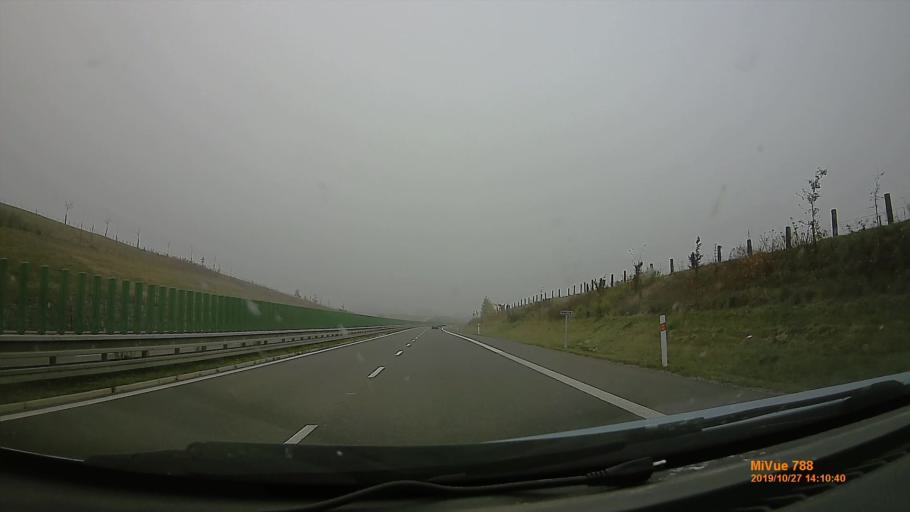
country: CZ
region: Olomoucky
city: Lestina
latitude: 49.8341
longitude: 16.9054
